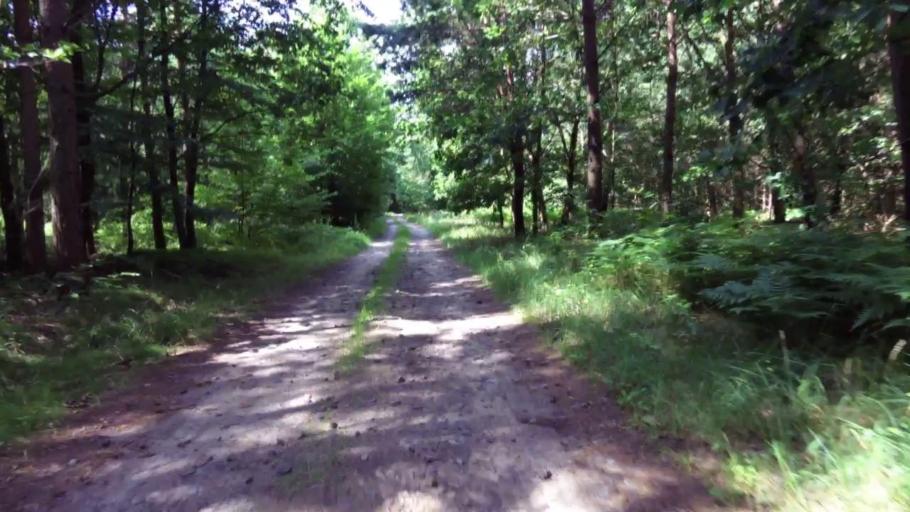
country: PL
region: West Pomeranian Voivodeship
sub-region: Powiat stargardzki
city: Kobylanka
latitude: 53.3483
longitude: 14.8344
